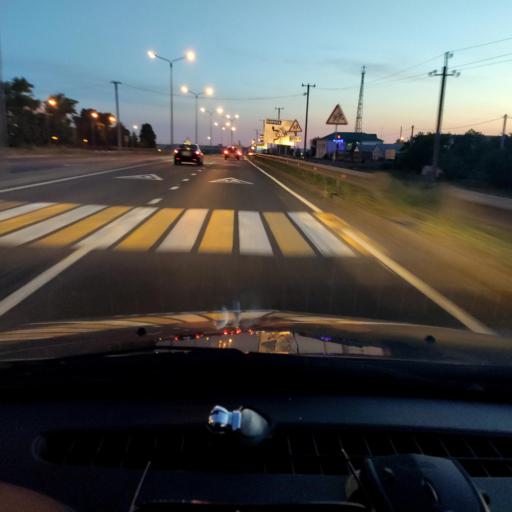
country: RU
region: Belgorod
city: Gubkin
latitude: 51.2611
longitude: 37.5343
